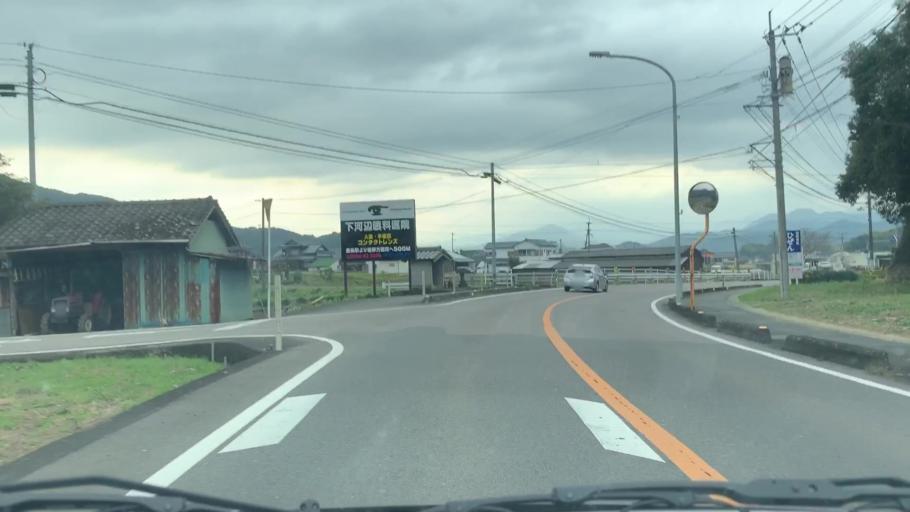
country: JP
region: Saga Prefecture
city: Kashima
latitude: 33.1521
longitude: 130.0648
